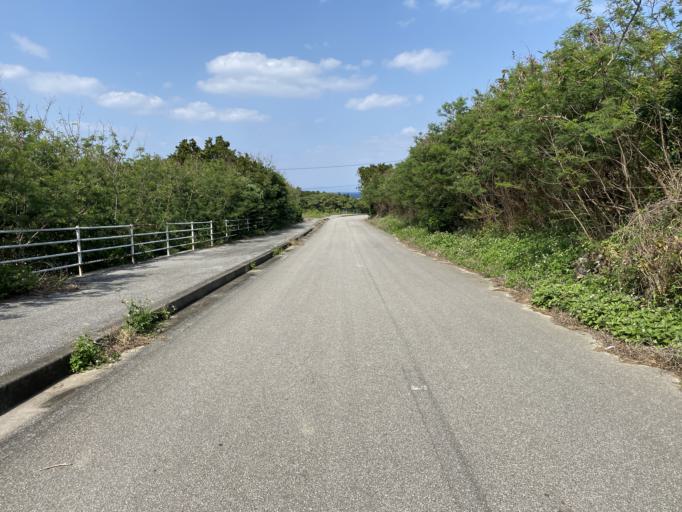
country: JP
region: Okinawa
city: Ishigaki
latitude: 24.0639
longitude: 123.7658
